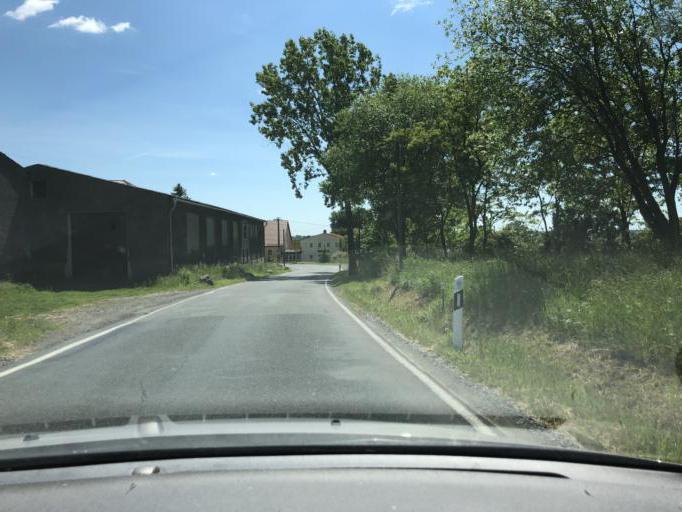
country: DE
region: Saxony
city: Nerchau
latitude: 51.2363
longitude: 12.8237
